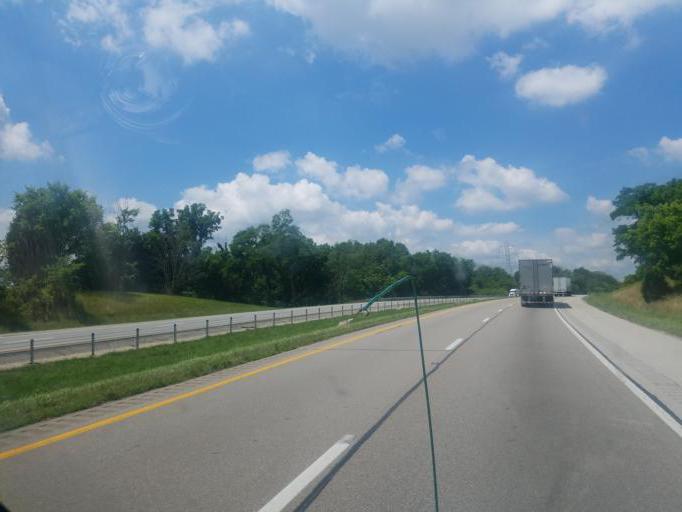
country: US
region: Kentucky
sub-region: Carroll County
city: Carrollton
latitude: 38.6524
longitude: -85.0871
